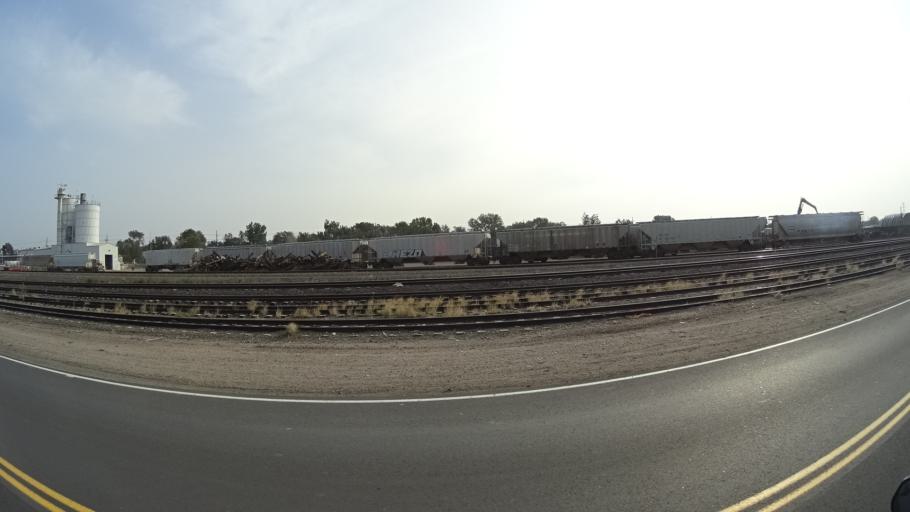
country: US
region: Colorado
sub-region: El Paso County
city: Stratmoor
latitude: 38.7918
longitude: -104.7781
